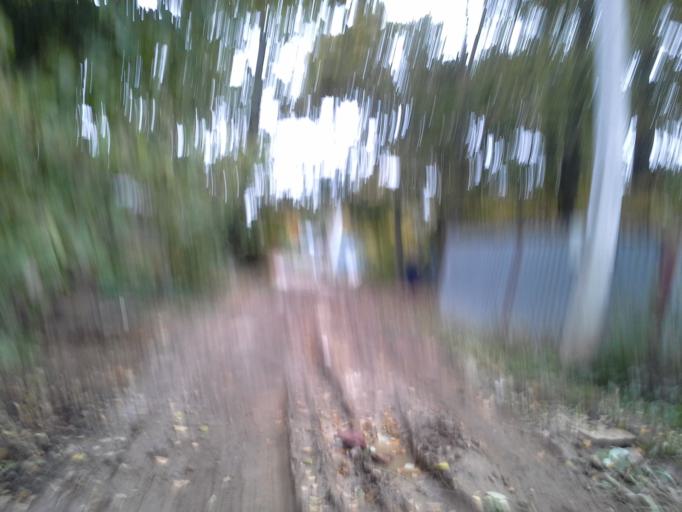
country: RU
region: Moskovskaya
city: Kokoshkino
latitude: 55.6224
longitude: 37.1594
